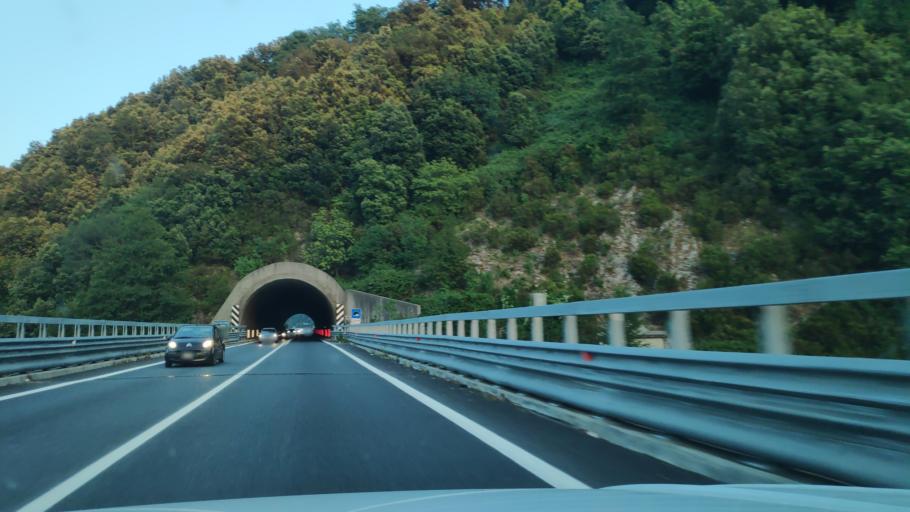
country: IT
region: Calabria
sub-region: Provincia di Reggio Calabria
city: Amato
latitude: 38.4099
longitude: 16.1439
